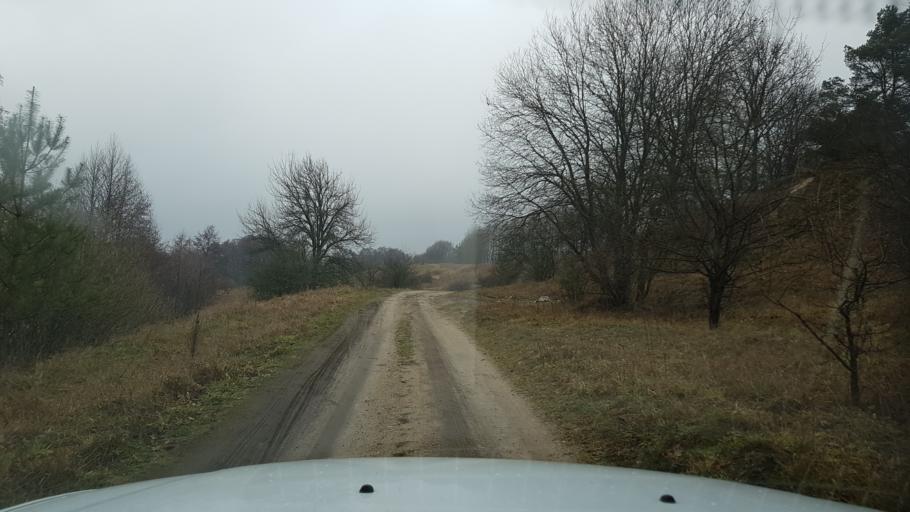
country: PL
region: West Pomeranian Voivodeship
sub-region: Powiat drawski
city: Czaplinek
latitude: 53.5648
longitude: 16.2471
